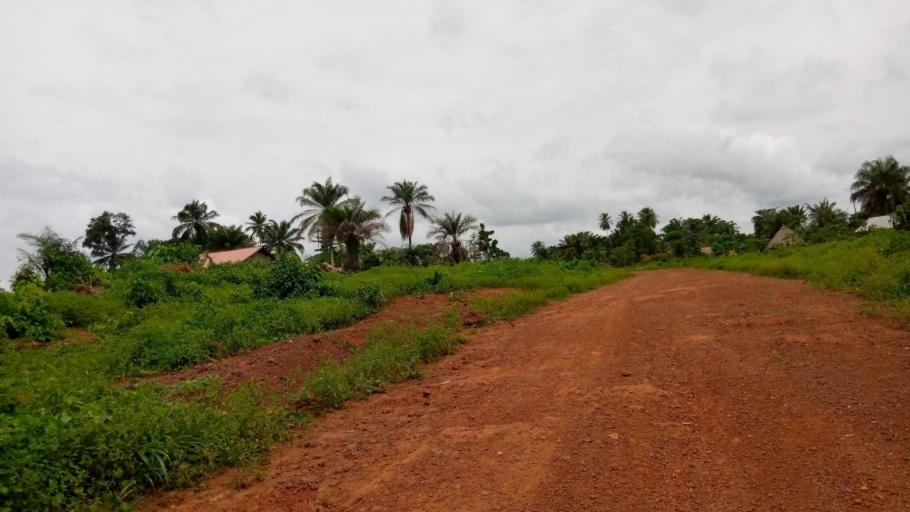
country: SL
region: Southern Province
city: Moyamba
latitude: 8.1748
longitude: -12.4988
